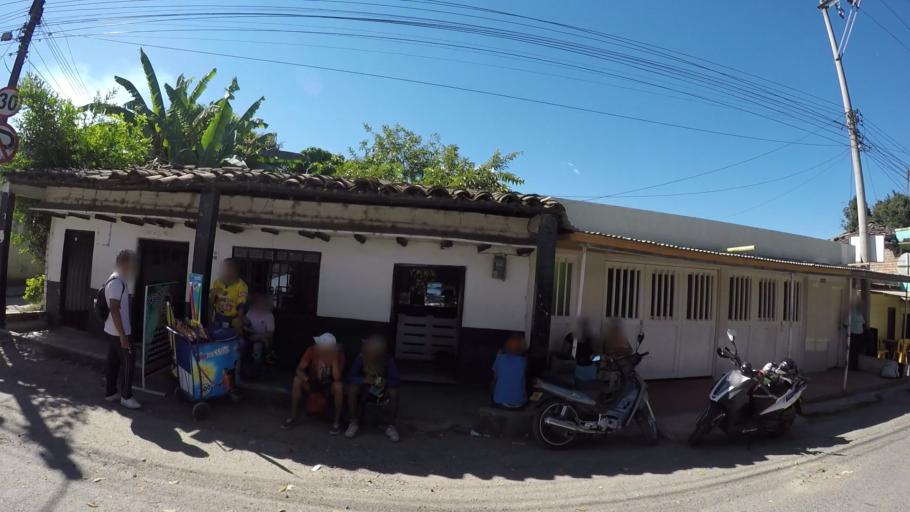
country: CO
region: Valle del Cauca
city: Cartago
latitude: 4.7593
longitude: -75.9000
